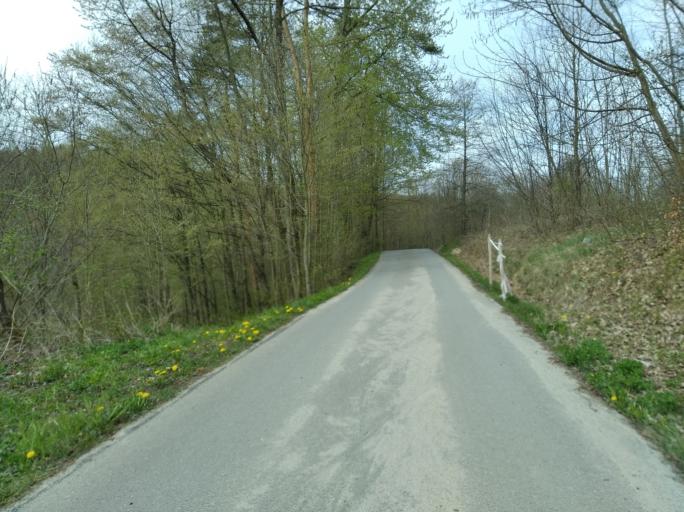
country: PL
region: Subcarpathian Voivodeship
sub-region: Powiat ropczycko-sedziszowski
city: Wielopole Skrzynskie
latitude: 49.9079
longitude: 21.6161
